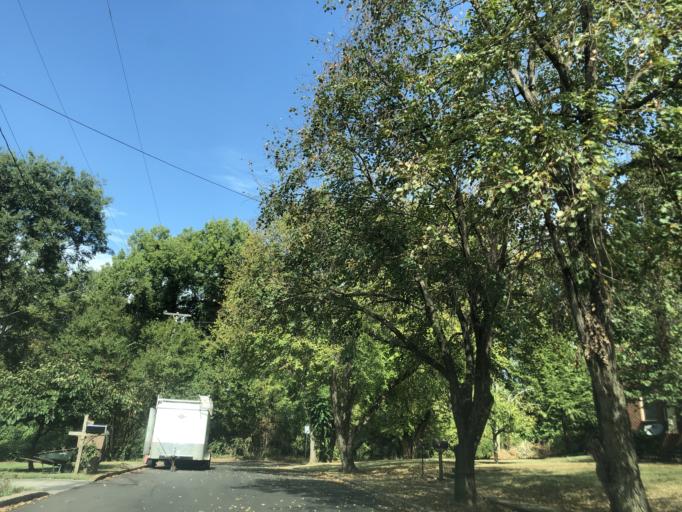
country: US
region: Tennessee
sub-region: Davidson County
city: Belle Meade
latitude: 36.1387
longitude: -86.8316
